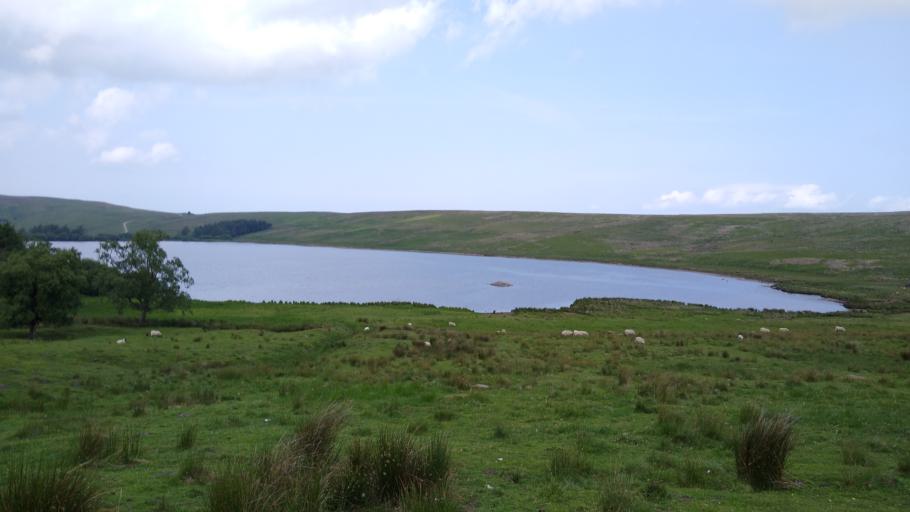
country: GB
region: England
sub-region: Northumberland
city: Greenhead
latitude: 54.9216
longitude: -2.6093
